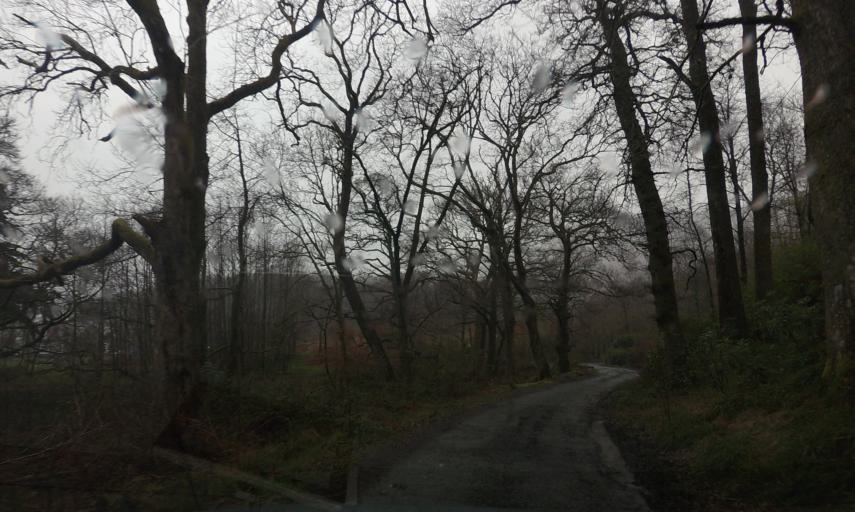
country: GB
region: Scotland
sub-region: West Dunbartonshire
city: Balloch
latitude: 56.1569
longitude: -4.6418
